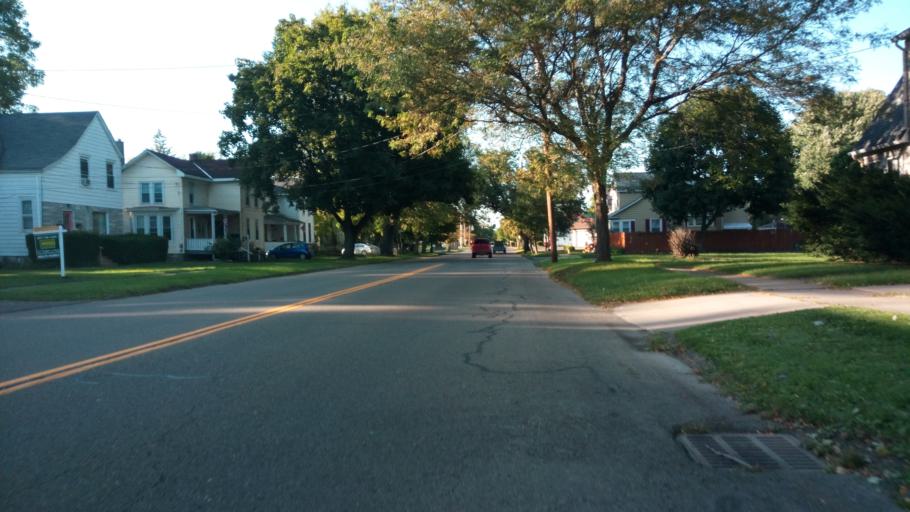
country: US
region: New York
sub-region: Chemung County
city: Elmira Heights
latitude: 42.1128
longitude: -76.8266
